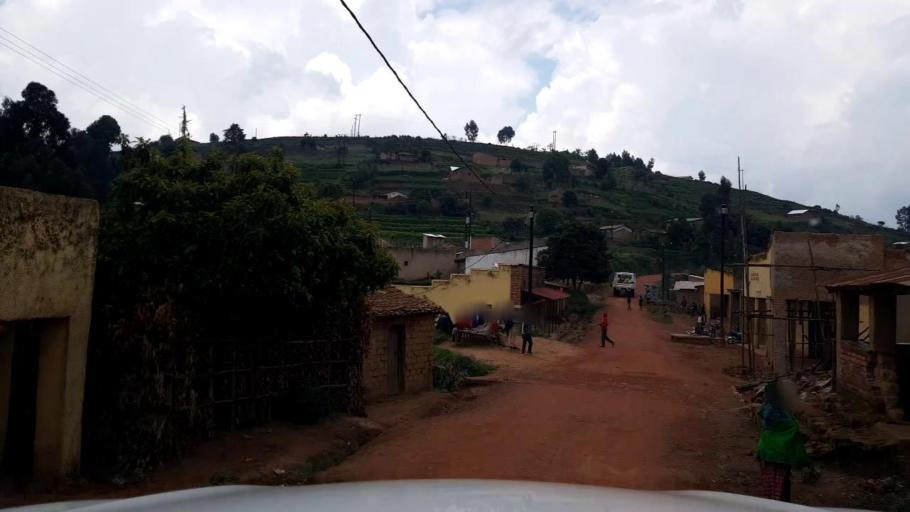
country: RW
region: Northern Province
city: Byumba
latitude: -1.5261
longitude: 29.9555
